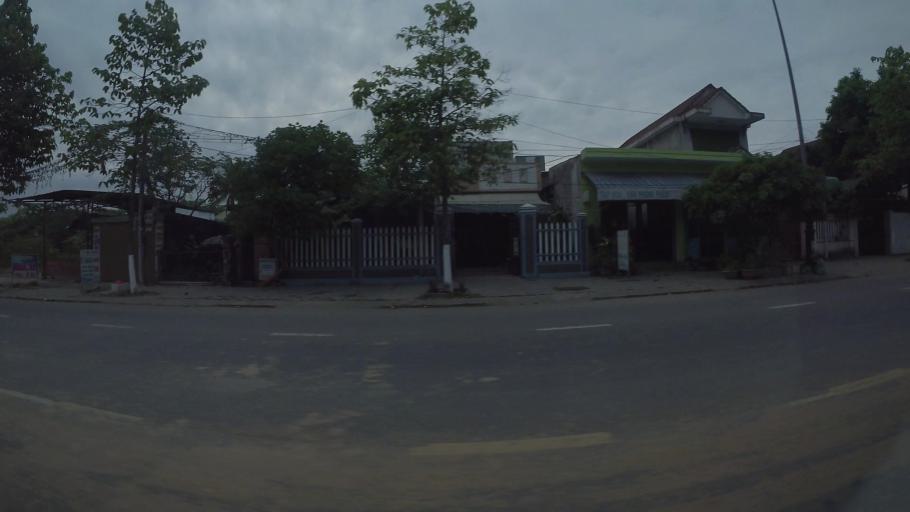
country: VN
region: Da Nang
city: Lien Chieu
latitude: 16.0734
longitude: 108.1109
